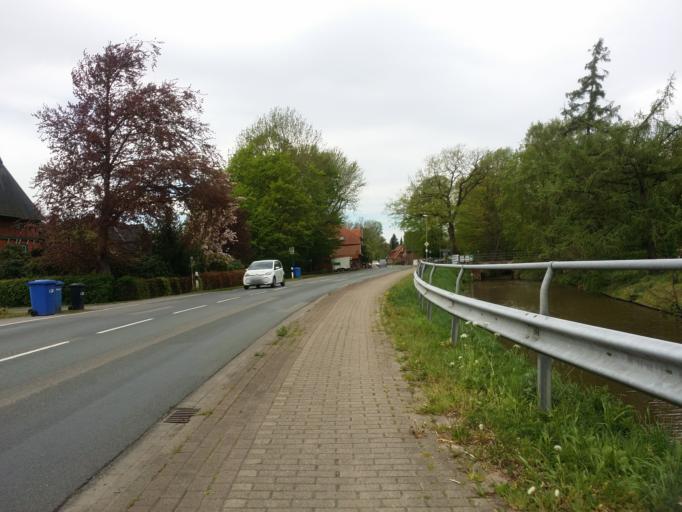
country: DE
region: Lower Saxony
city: Lemwerder
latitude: 53.1404
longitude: 8.5754
